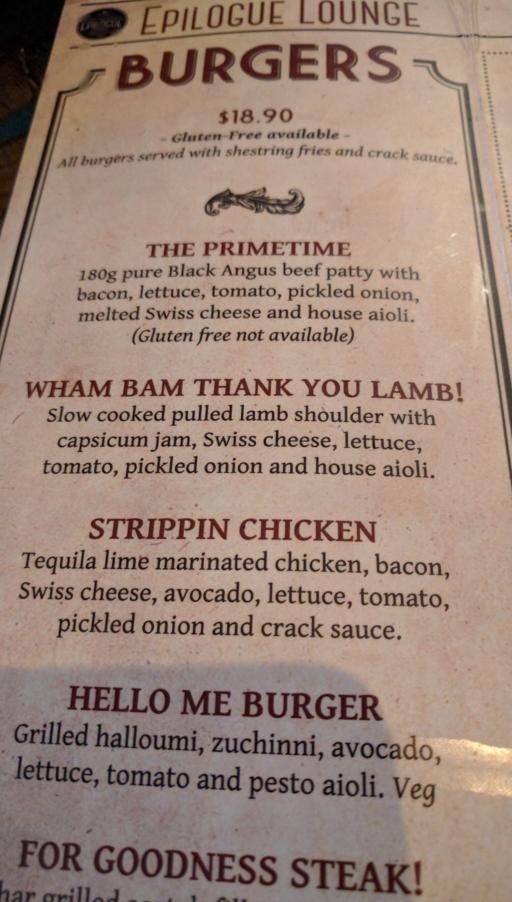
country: AU
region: Northern Territory
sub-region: Alice Springs
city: Alice Springs
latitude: -23.7004
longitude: 133.8823
